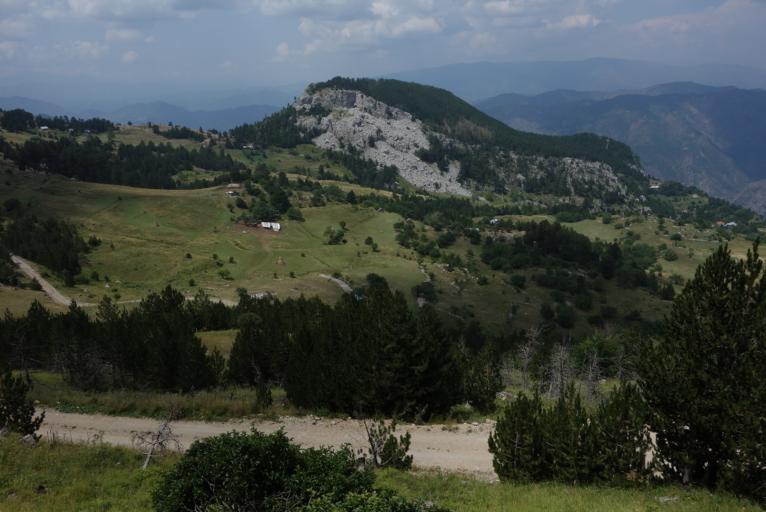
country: AL
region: Lezhe
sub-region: Rrethi i Mirdites
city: Orosh
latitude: 41.8615
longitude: 20.1205
